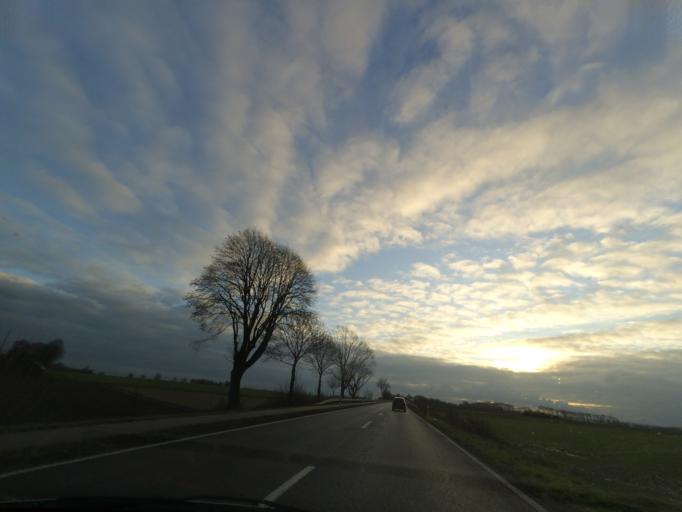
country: DE
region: North Rhine-Westphalia
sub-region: Regierungsbezirk Dusseldorf
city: Grevenbroich
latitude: 51.1126
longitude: 6.5567
